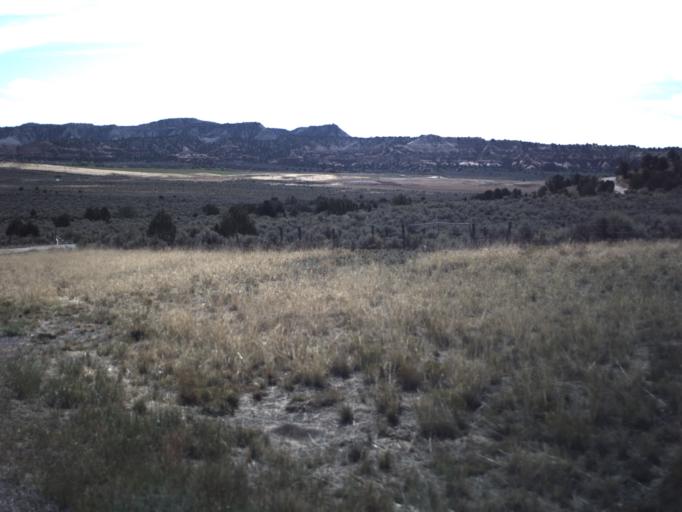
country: US
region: Utah
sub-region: Garfield County
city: Panguitch
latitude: 37.5634
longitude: -112.0355
